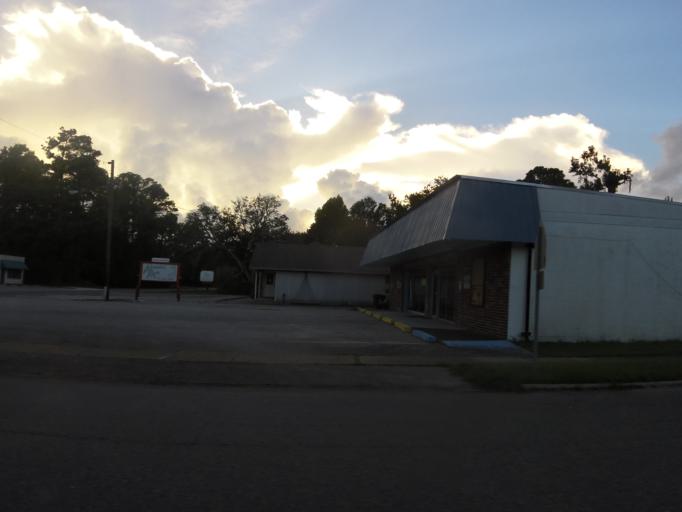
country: US
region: Georgia
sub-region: Camden County
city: St. Marys
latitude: 30.7293
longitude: -81.5466
